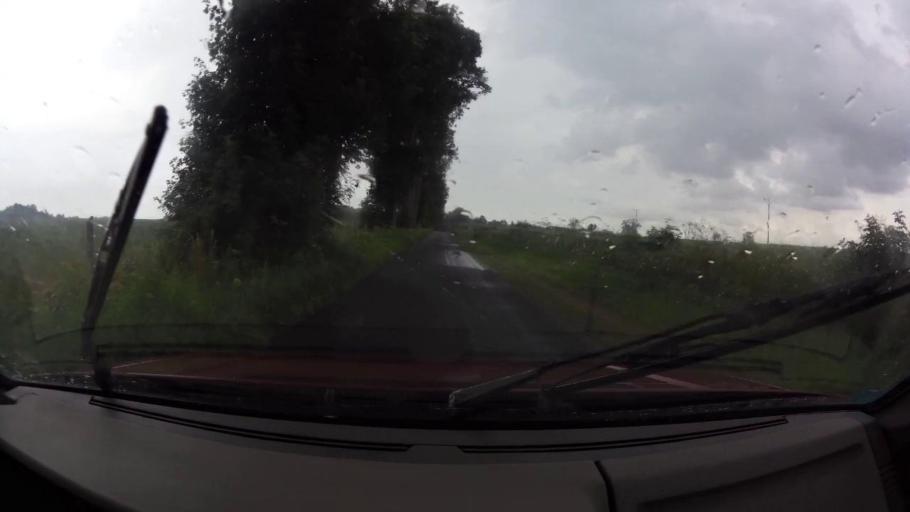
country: PL
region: West Pomeranian Voivodeship
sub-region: Koszalin
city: Koszalin
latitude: 54.0833
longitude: 16.1265
